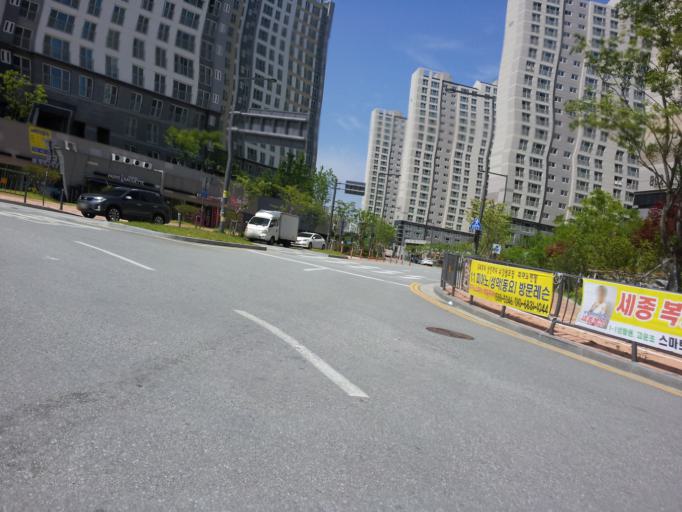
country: KR
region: Chungcheongnam-do
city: Gongju
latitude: 36.5056
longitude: 127.2389
